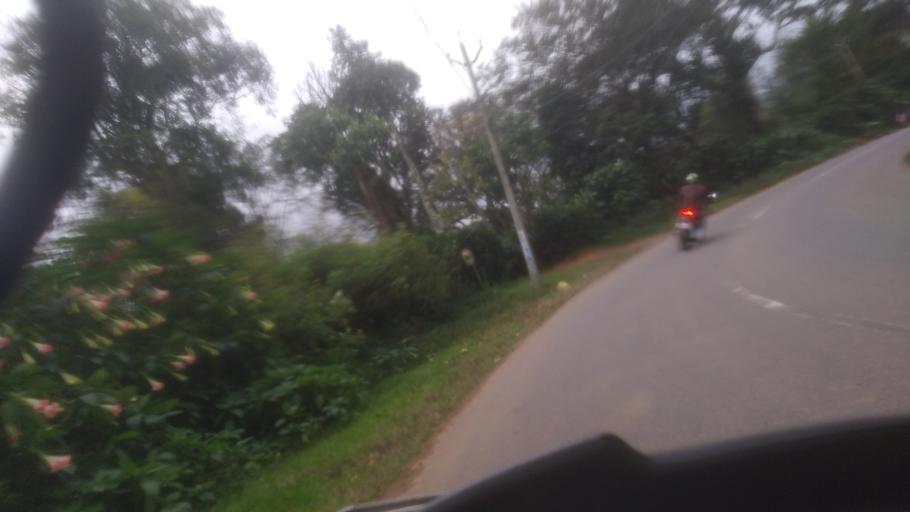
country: IN
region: Tamil Nadu
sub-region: Theni
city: Kombai
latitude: 9.8941
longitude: 77.1713
